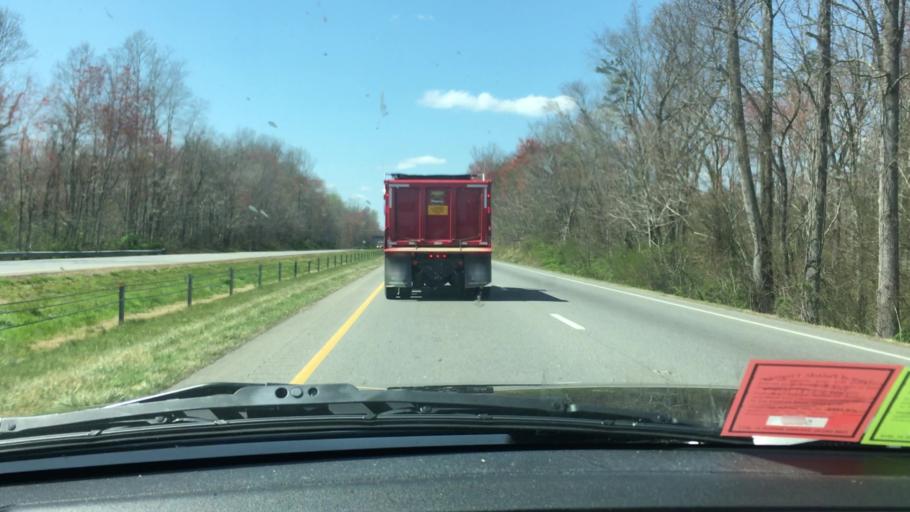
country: US
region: North Carolina
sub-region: Surry County
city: Pilot Mountain
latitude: 36.4323
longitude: -80.5281
